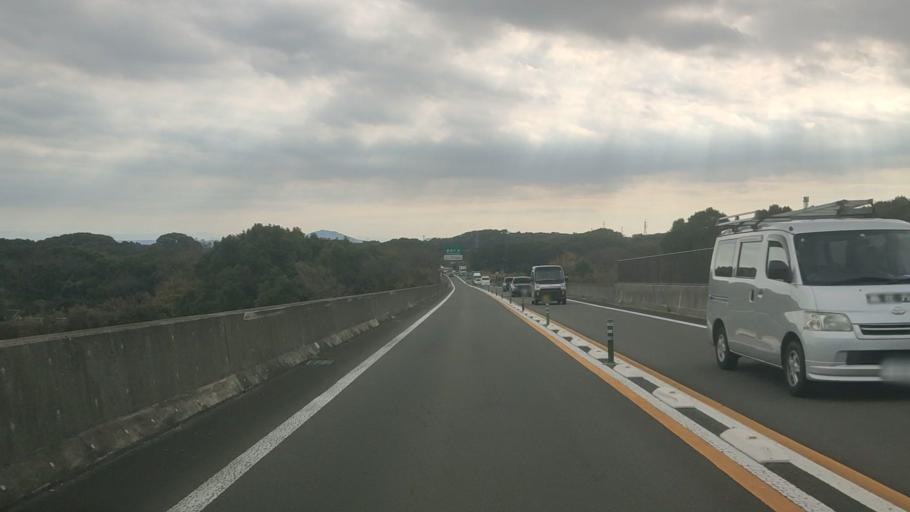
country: JP
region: Nagasaki
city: Shimabara
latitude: 32.7687
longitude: 130.3588
